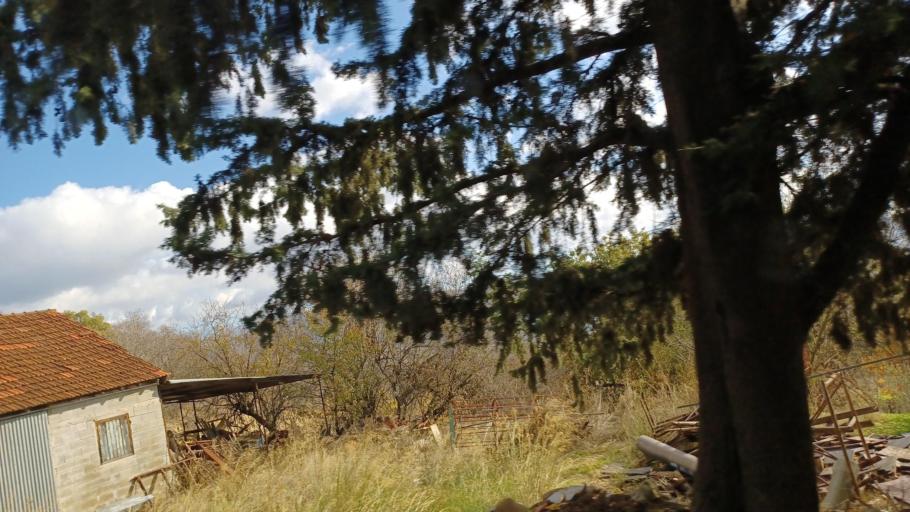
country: CY
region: Limassol
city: Pachna
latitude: 34.8425
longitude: 32.6925
